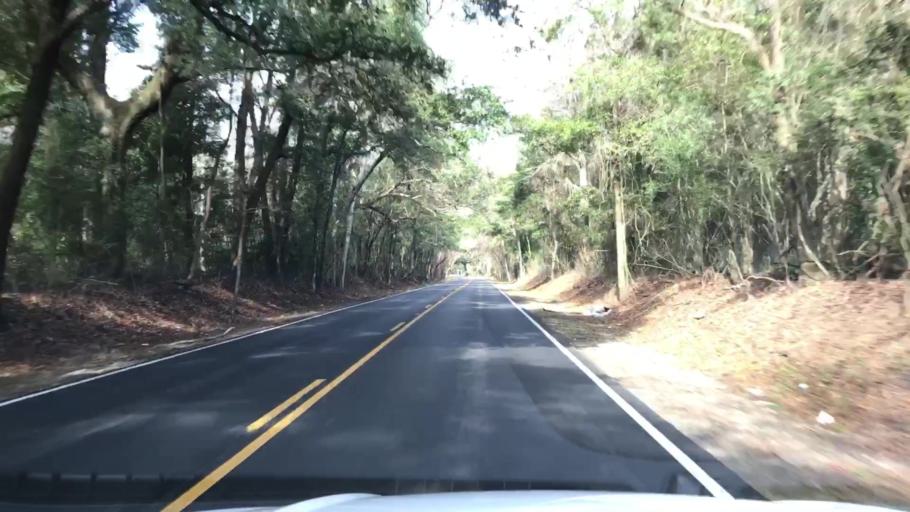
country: US
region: South Carolina
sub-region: Charleston County
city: Folly Beach
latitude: 32.7114
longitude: -80.0181
